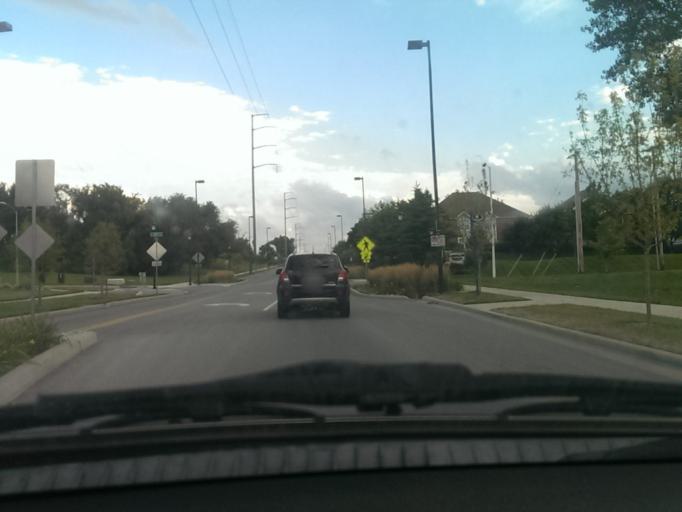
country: US
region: Missouri
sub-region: Jackson County
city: Kansas City
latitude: 39.0819
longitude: -94.5708
